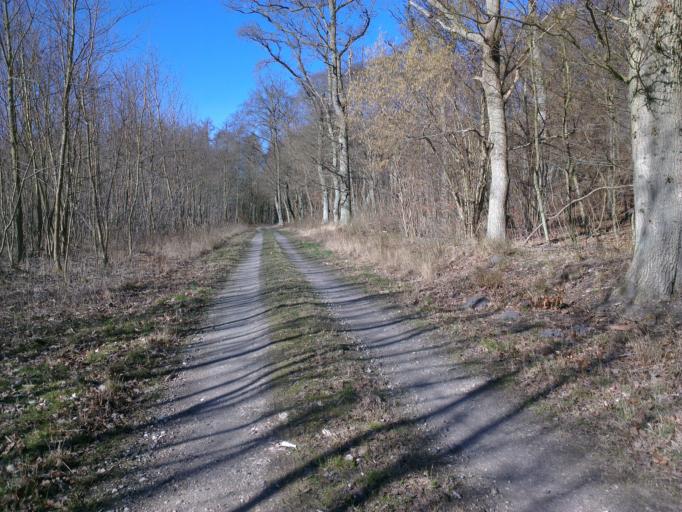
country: DK
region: Capital Region
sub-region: Frederikssund Kommune
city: Jaegerspris
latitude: 55.8910
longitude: 11.9971
